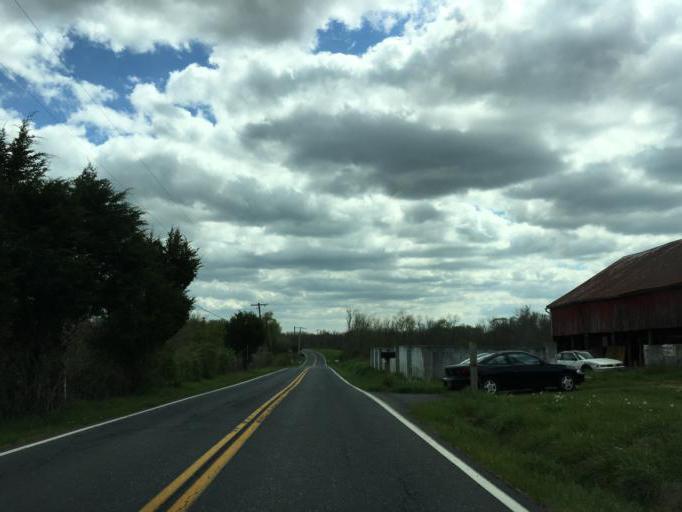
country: US
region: Maryland
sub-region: Frederick County
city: Thurmont
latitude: 39.5874
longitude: -77.3927
